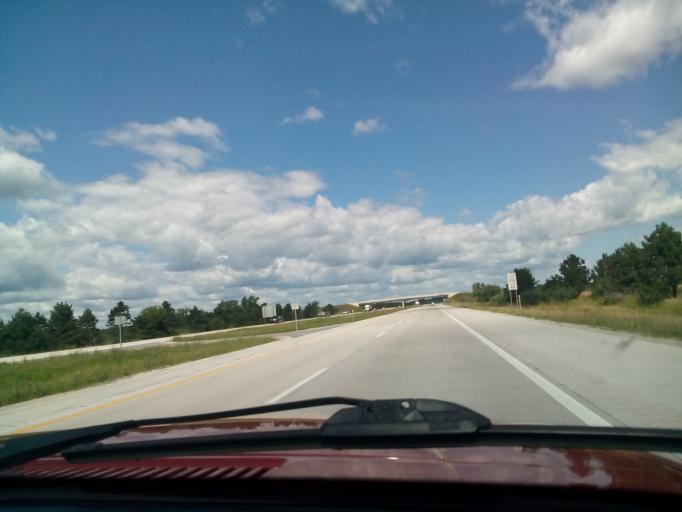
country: US
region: Michigan
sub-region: Bay County
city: Pinconning
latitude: 43.8645
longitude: -84.0209
